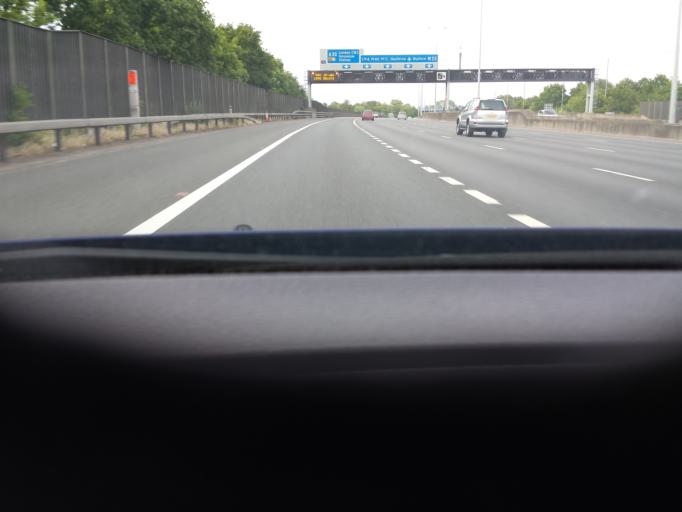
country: GB
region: England
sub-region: Surrey
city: Egham
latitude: 51.4338
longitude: -0.5387
